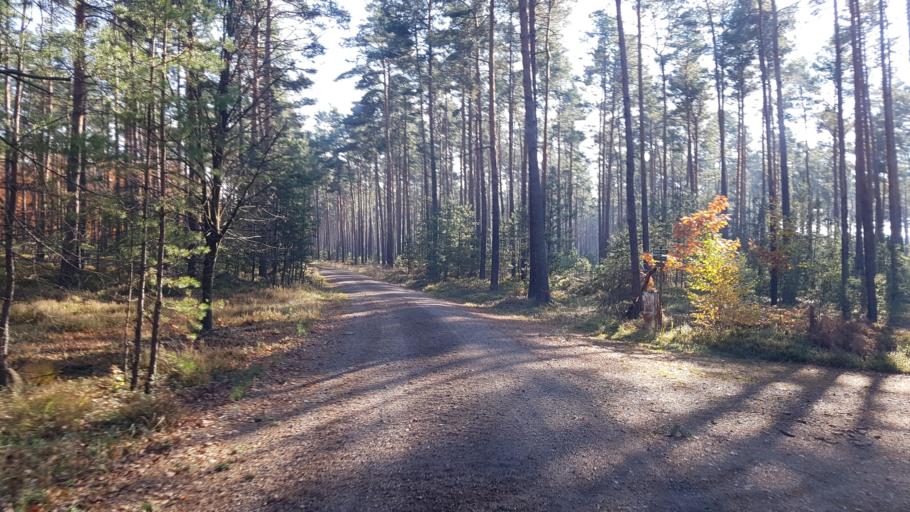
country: DE
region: Brandenburg
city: Ruckersdorf
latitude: 51.5704
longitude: 13.6110
